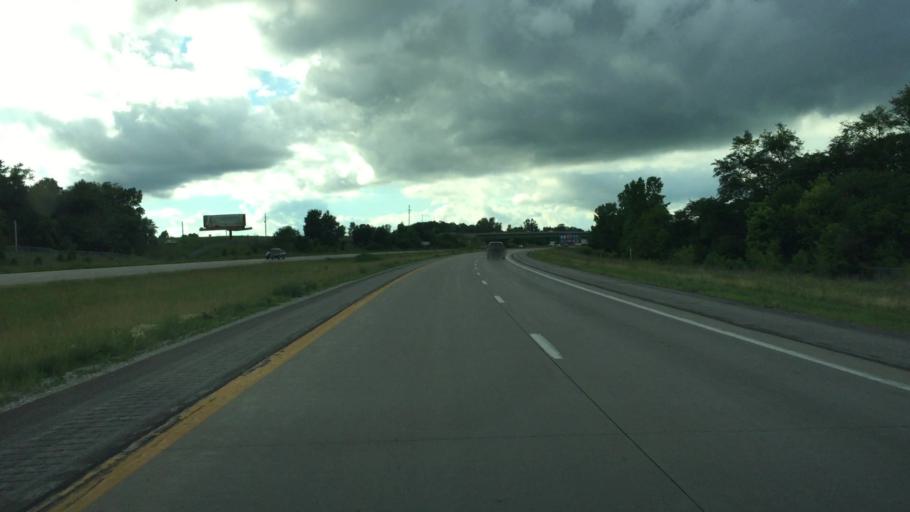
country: US
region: Iowa
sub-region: Polk County
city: Altoona
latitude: 41.6286
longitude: -93.4996
